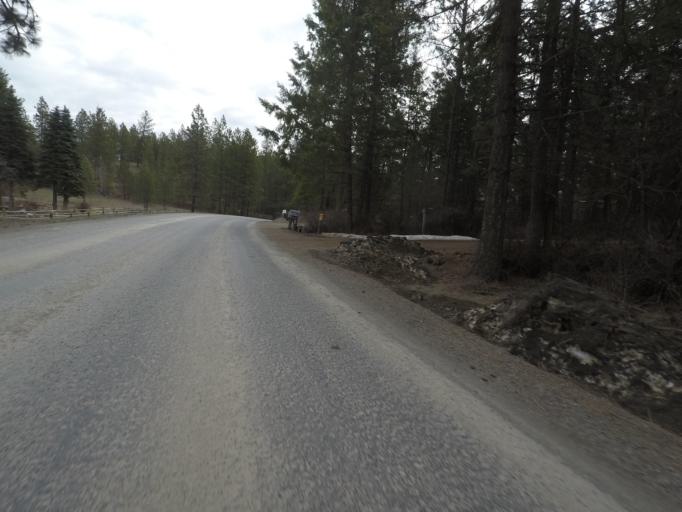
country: US
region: Washington
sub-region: Stevens County
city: Colville
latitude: 48.5037
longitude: -117.8536
